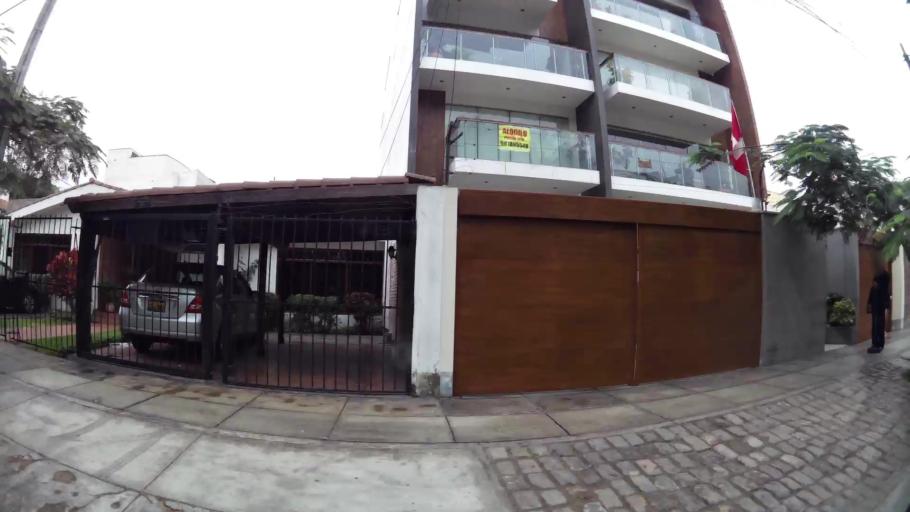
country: PE
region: Lima
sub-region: Lima
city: Surco
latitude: -12.1335
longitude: -77.0110
